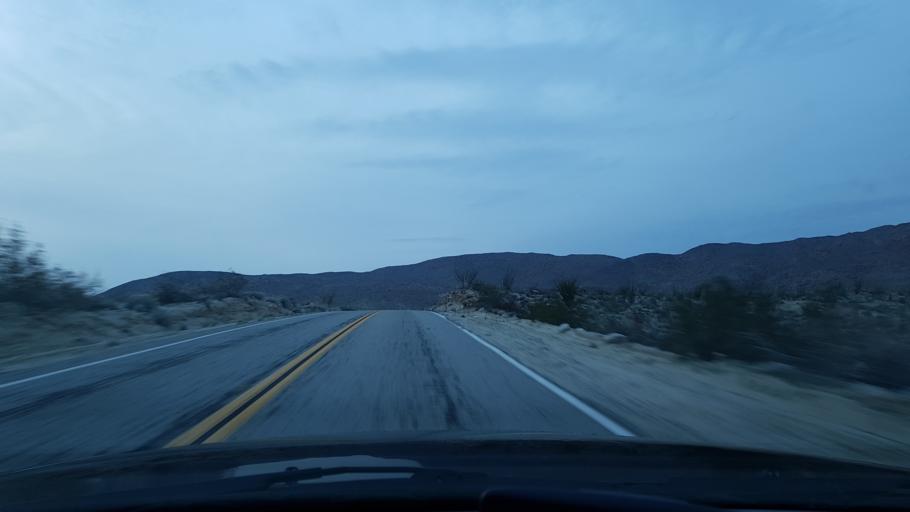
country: US
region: California
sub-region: San Diego County
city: Pine Valley
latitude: 32.9741
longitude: -116.3442
